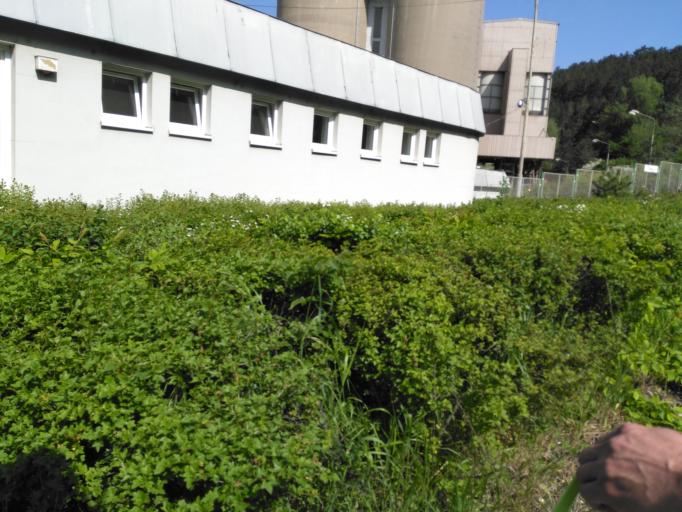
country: CZ
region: Central Bohemia
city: Cernosice
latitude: 49.9954
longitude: 14.3428
